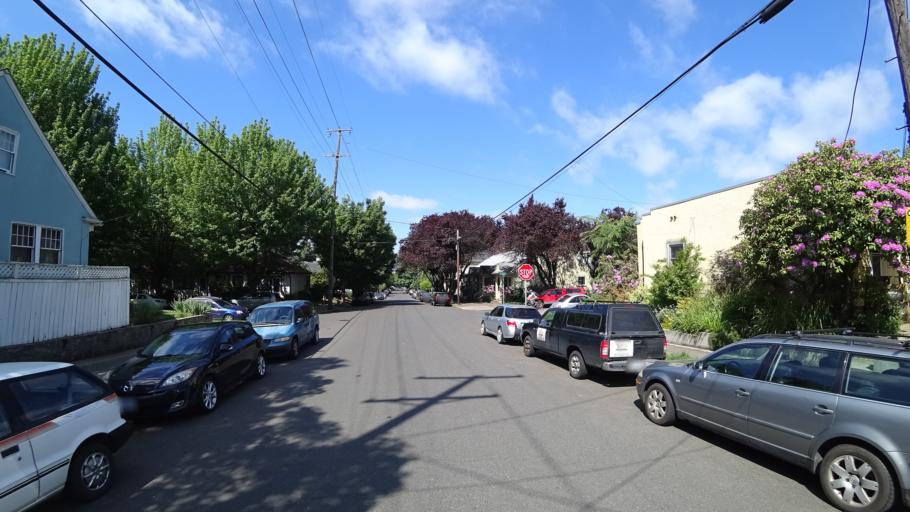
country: US
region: Oregon
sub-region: Multnomah County
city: Portland
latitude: 45.5129
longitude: -122.6412
